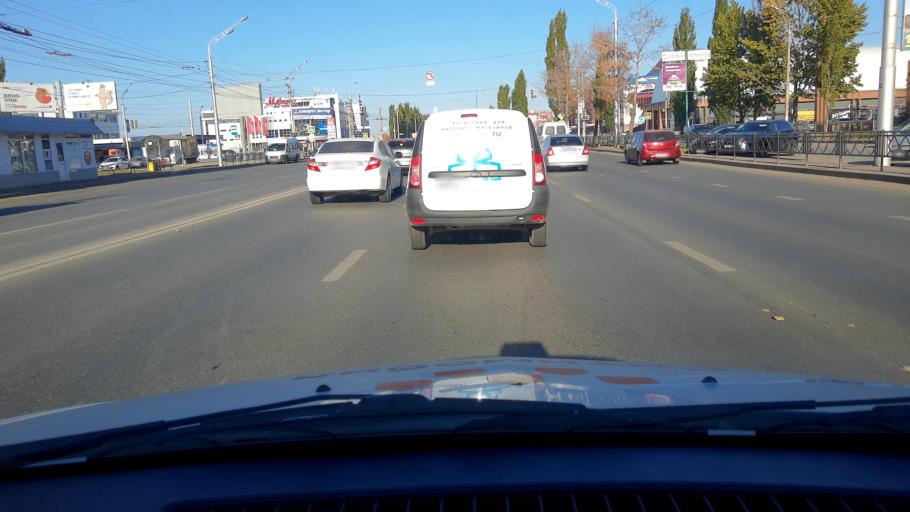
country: RU
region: Bashkortostan
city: Ufa
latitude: 54.7688
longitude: 56.0556
